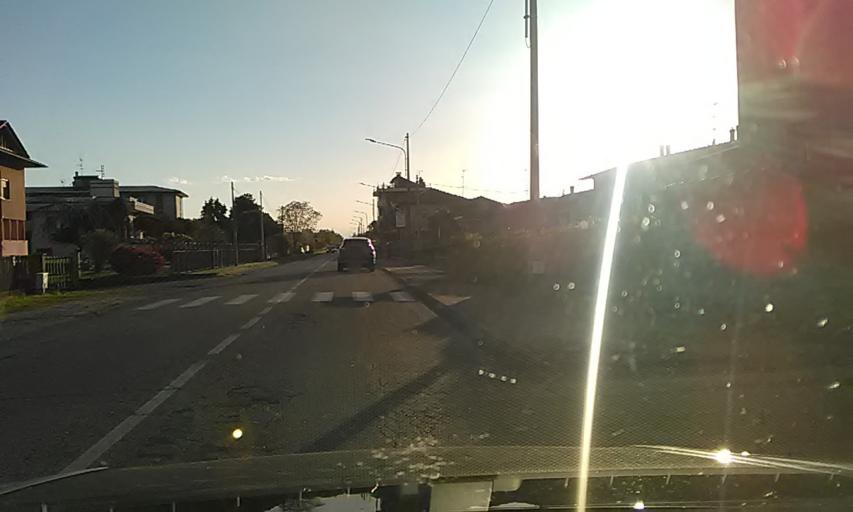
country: IT
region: Piedmont
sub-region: Provincia di Novara
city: Carpignano Sesia
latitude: 45.5325
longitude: 8.4125
